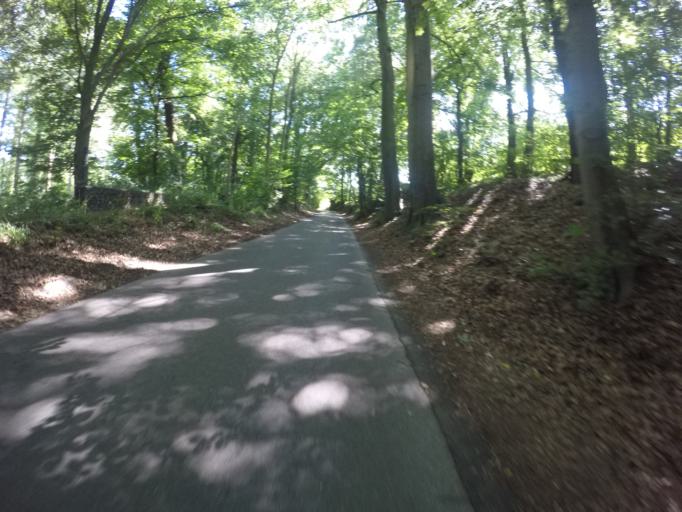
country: DE
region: North Rhine-Westphalia
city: Bad Oeynhausen
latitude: 52.1937
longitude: 8.7881
